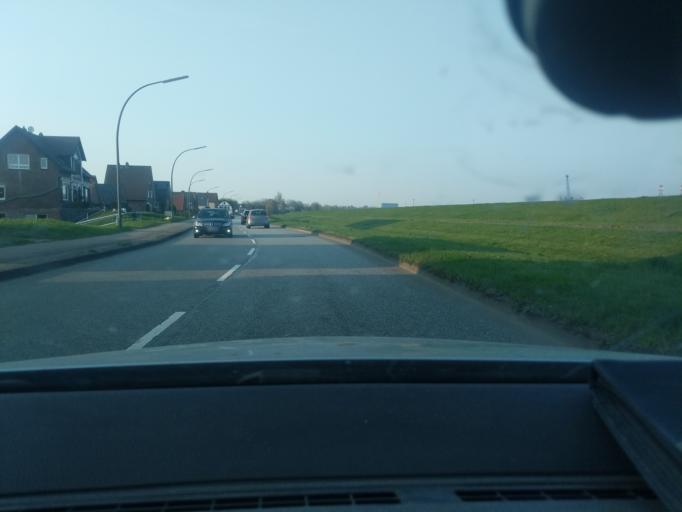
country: DE
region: Hamburg
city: Altona
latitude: 53.5213
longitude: 9.8868
